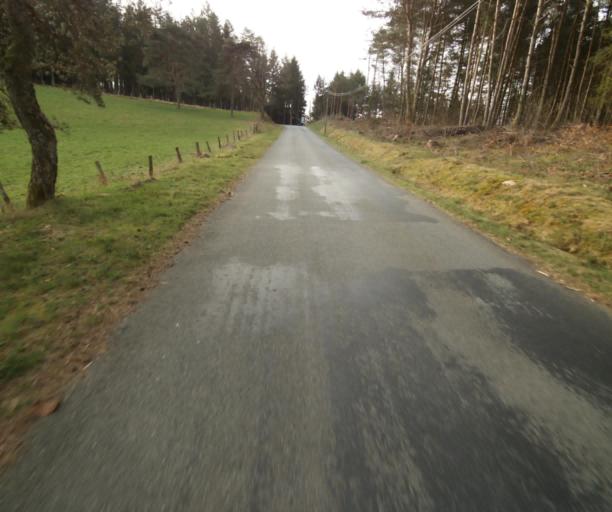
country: FR
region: Limousin
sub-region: Departement de la Correze
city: Treignac
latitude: 45.4625
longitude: 1.8139
